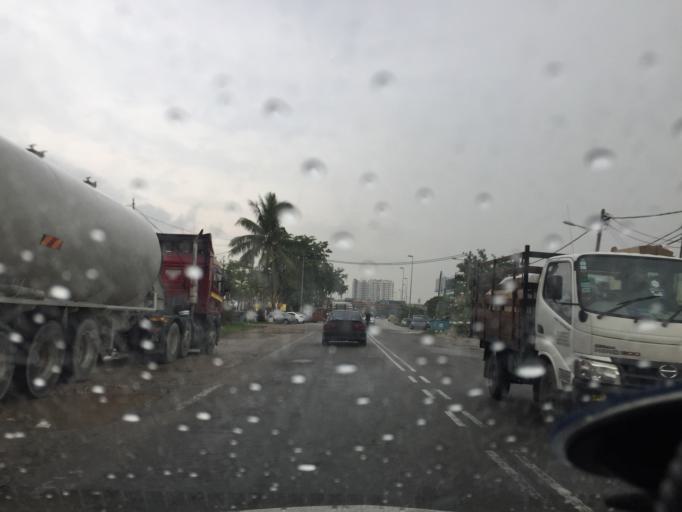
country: MY
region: Selangor
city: Subang Jaya
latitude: 3.0170
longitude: 101.5301
